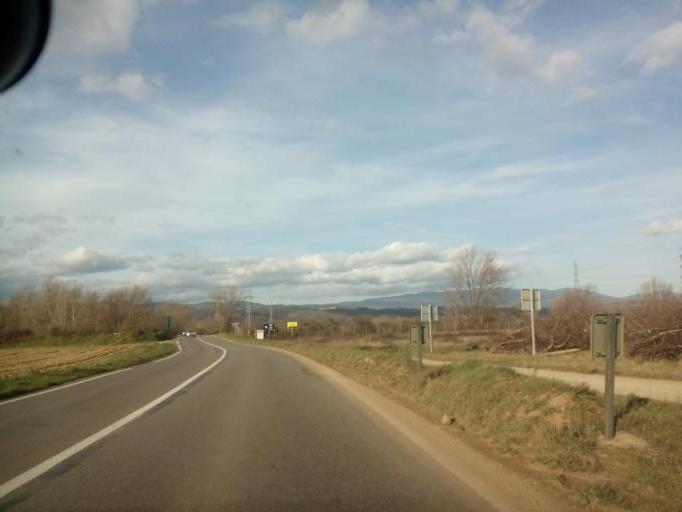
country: FR
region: Rhone-Alpes
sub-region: Departement de l'Isere
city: Chanas
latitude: 45.3185
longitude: 4.8048
